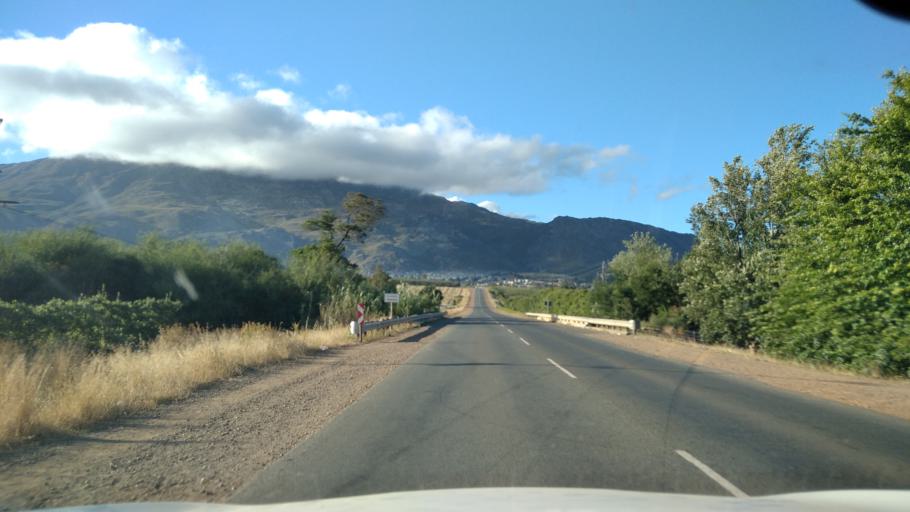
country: ZA
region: Western Cape
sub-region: Overberg District Municipality
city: Caledon
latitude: -34.0068
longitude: 19.2919
